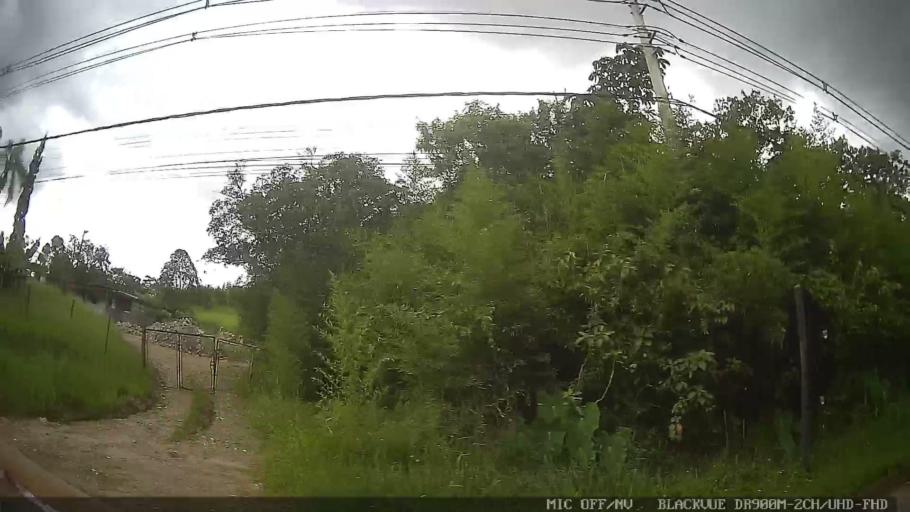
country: BR
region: Sao Paulo
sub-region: Suzano
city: Suzano
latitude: -23.6011
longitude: -46.3063
